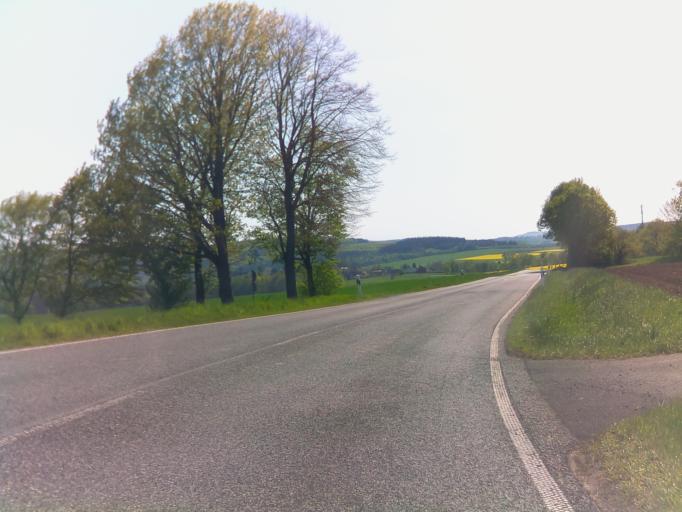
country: DE
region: Hesse
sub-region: Regierungsbezirk Darmstadt
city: Birstein
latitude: 50.3949
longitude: 9.3097
